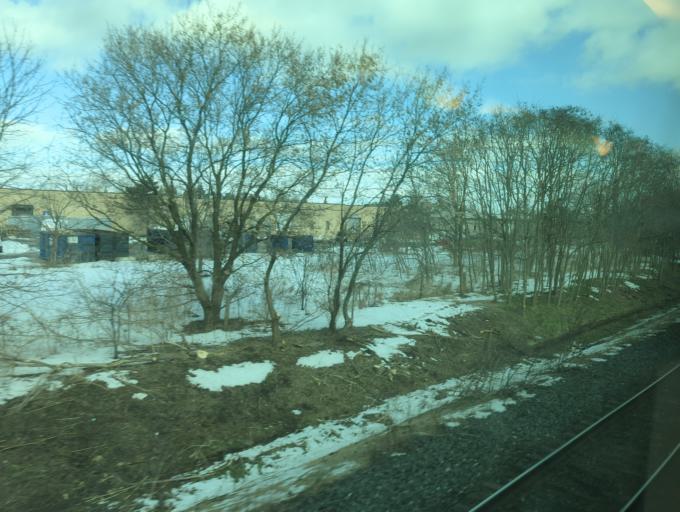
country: CA
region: Ontario
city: Burlington
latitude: 43.3559
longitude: -79.7859
